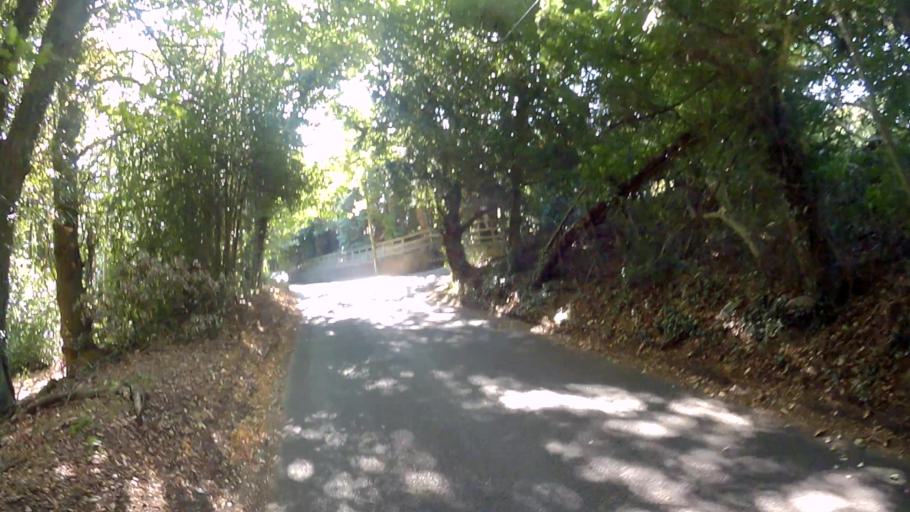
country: GB
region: England
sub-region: Surrey
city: Churt
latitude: 51.1755
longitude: -0.7861
